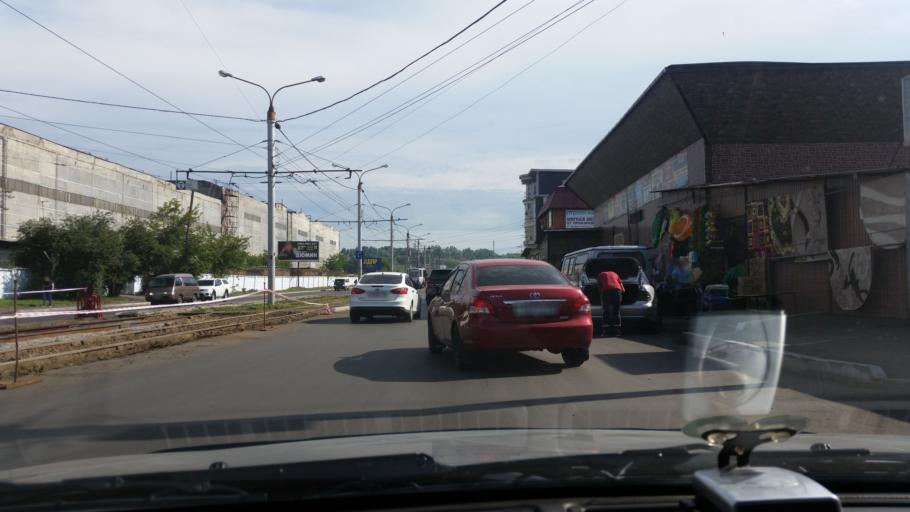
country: RU
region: Irkutsk
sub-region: Irkutskiy Rayon
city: Irkutsk
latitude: 52.2890
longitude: 104.3077
